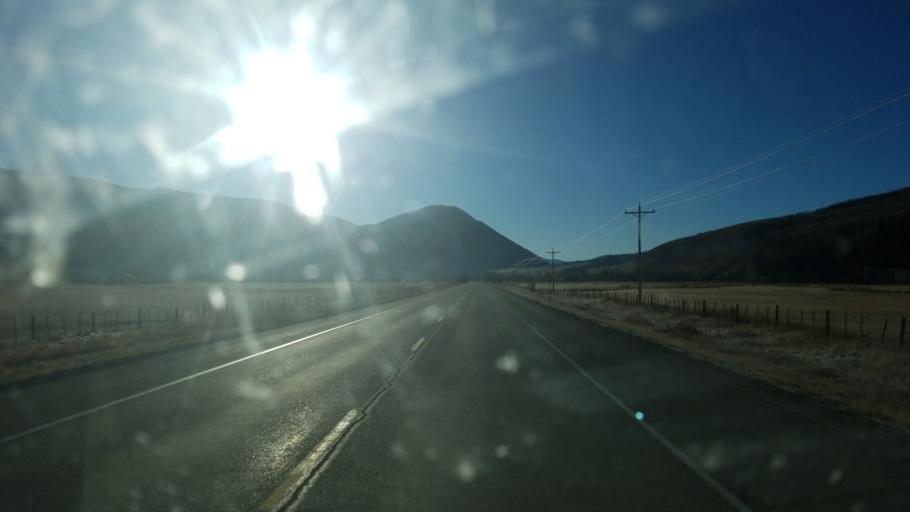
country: US
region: Colorado
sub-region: Gunnison County
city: Crested Butte
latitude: 38.8216
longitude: -106.9140
